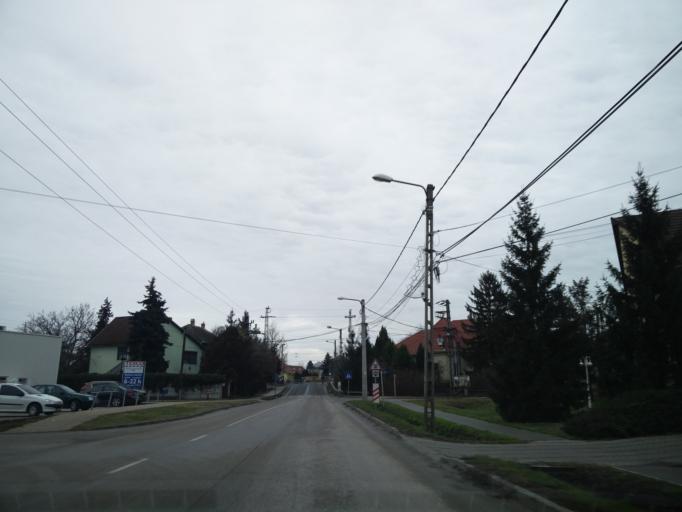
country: HU
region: Pest
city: Suelysap
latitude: 47.4510
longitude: 19.5344
